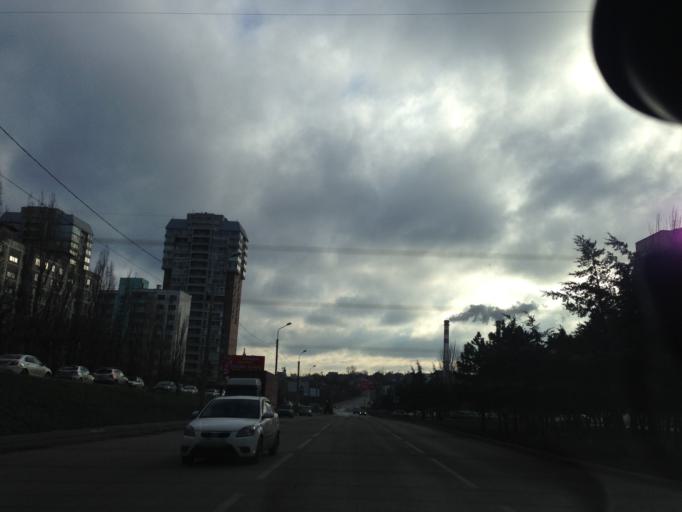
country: RU
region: Rostov
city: Severnyy
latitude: 47.2908
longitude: 39.6951
